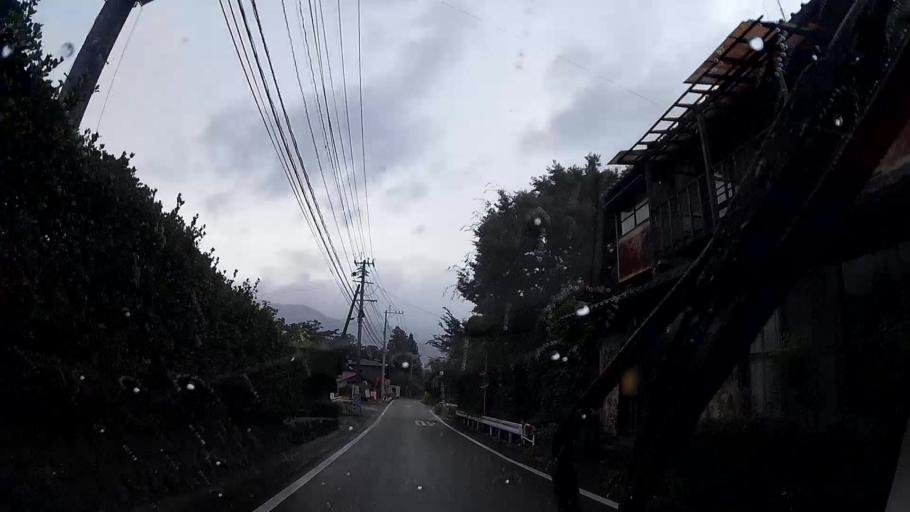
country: JP
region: Kumamoto
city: Aso
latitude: 32.8430
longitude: 131.0304
